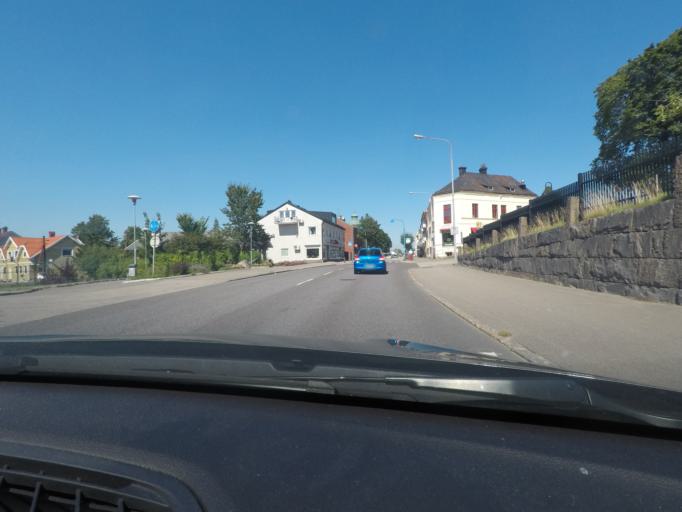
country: SE
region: Kronoberg
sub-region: Markaryds Kommun
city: Markaryd
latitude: 56.4606
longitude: 13.5951
